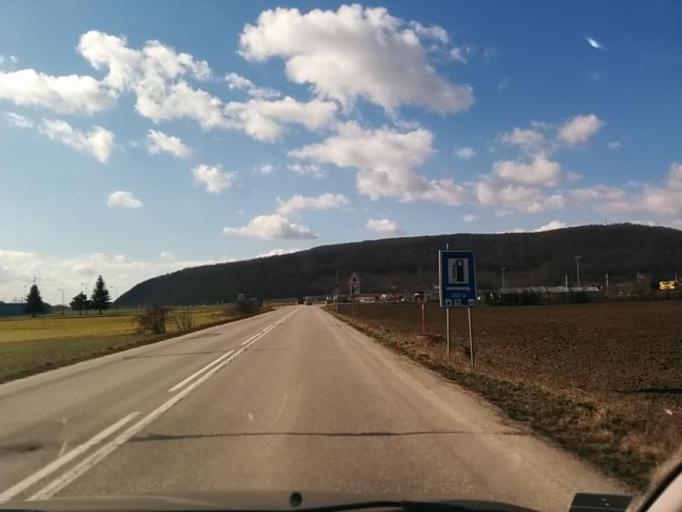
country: SK
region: Trenciansky
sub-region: Okres Nove Mesto nad Vahom
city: Nove Mesto nad Vahom
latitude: 48.8008
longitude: 17.8763
